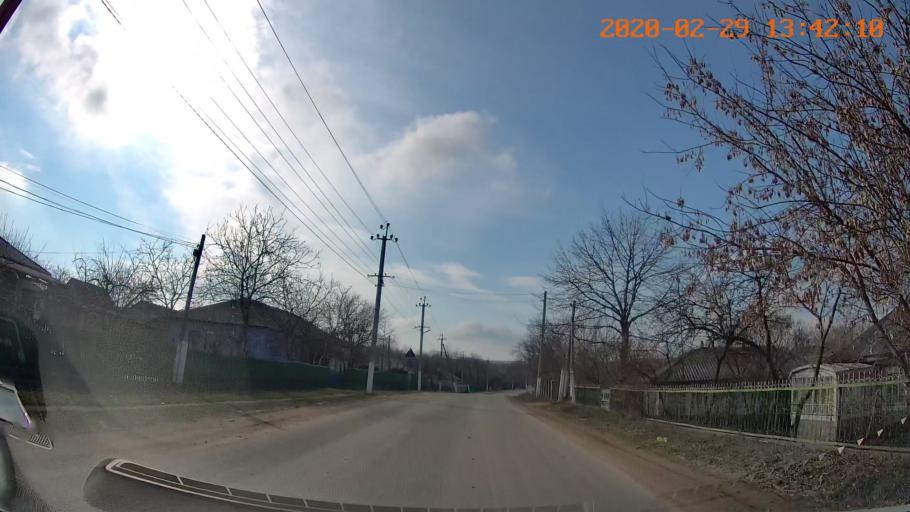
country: MD
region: Floresti
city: Leninskiy
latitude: 47.8423
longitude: 28.5516
